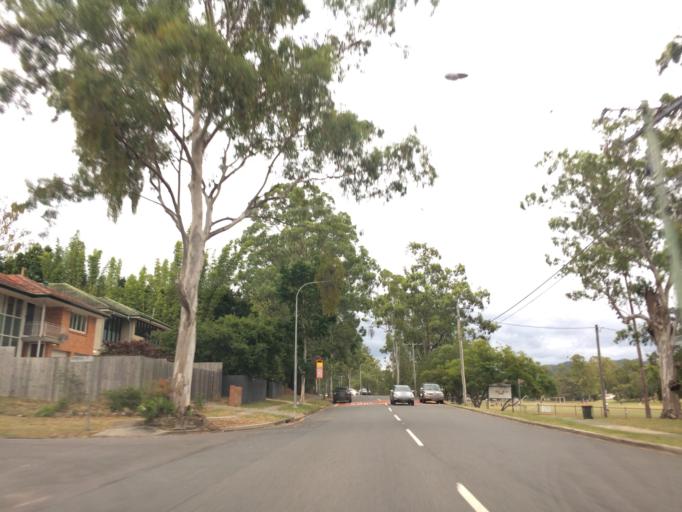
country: AU
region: Queensland
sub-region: Brisbane
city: Taringa
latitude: -27.5030
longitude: 152.9875
